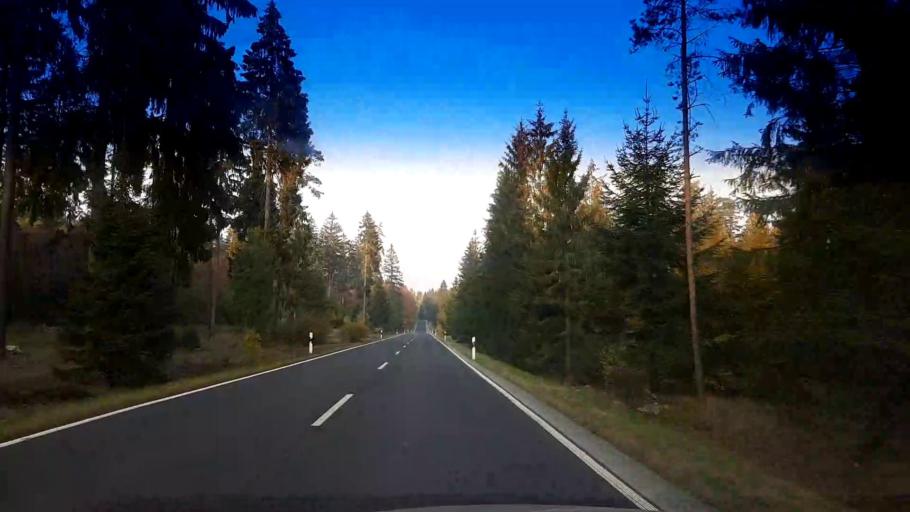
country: DE
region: Bavaria
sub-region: Upper Franconia
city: Schirnding
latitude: 50.0580
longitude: 12.2446
